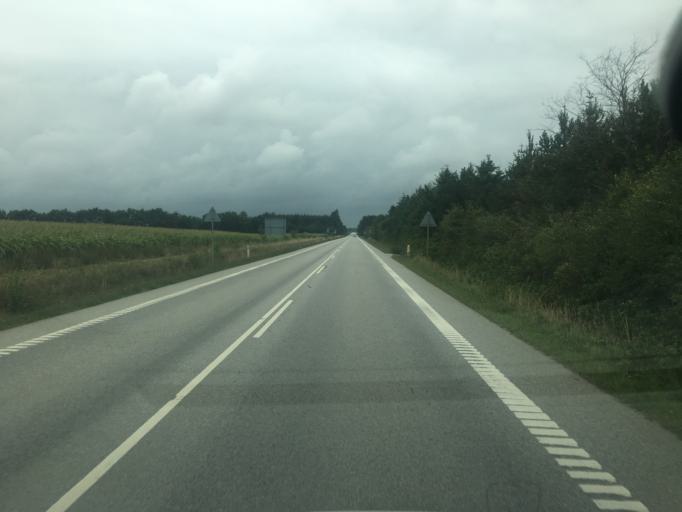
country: DK
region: South Denmark
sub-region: Haderslev Kommune
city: Vojens
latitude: 55.2203
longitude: 9.3015
